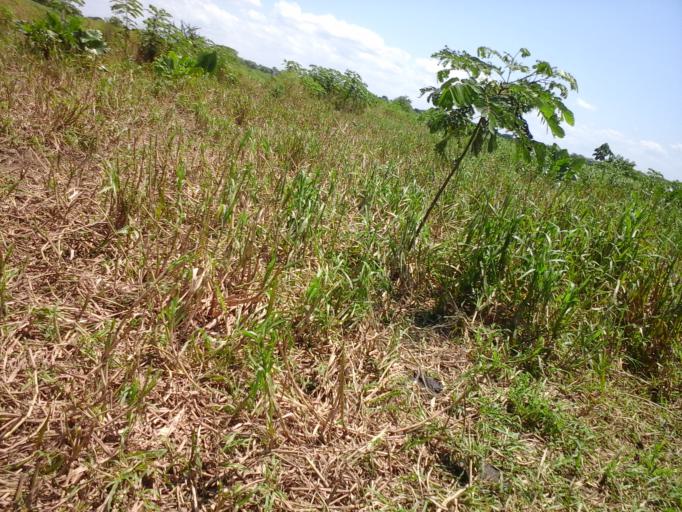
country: CO
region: Bolivar
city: Mahates
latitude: 10.1660
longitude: -75.2744
